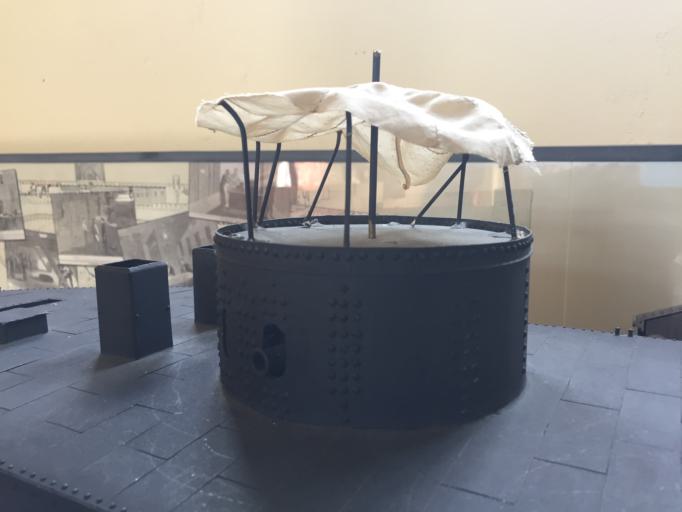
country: SE
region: Vaermland
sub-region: Filipstads Kommun
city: Lesjofors
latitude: 59.8543
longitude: 14.2611
